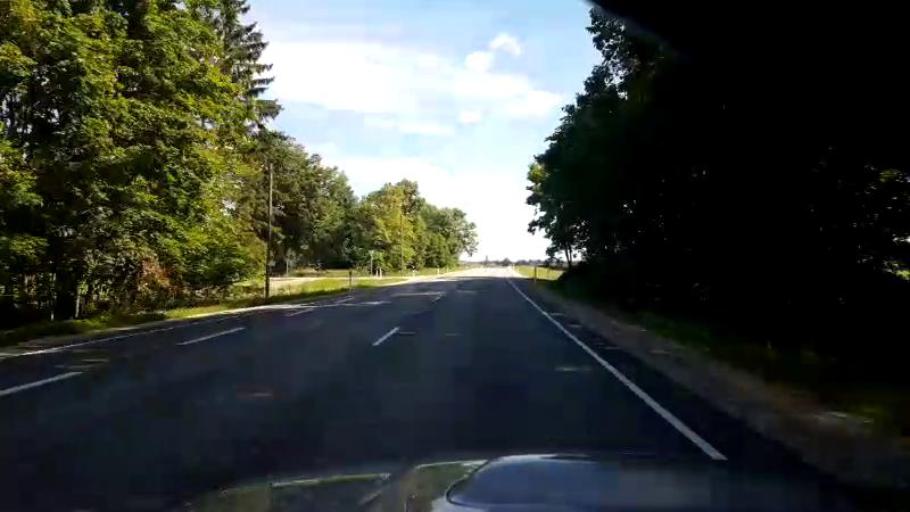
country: EE
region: Jaervamaa
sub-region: Jaerva-Jaani vald
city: Jarva-Jaani
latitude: 59.0976
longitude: 25.6986
